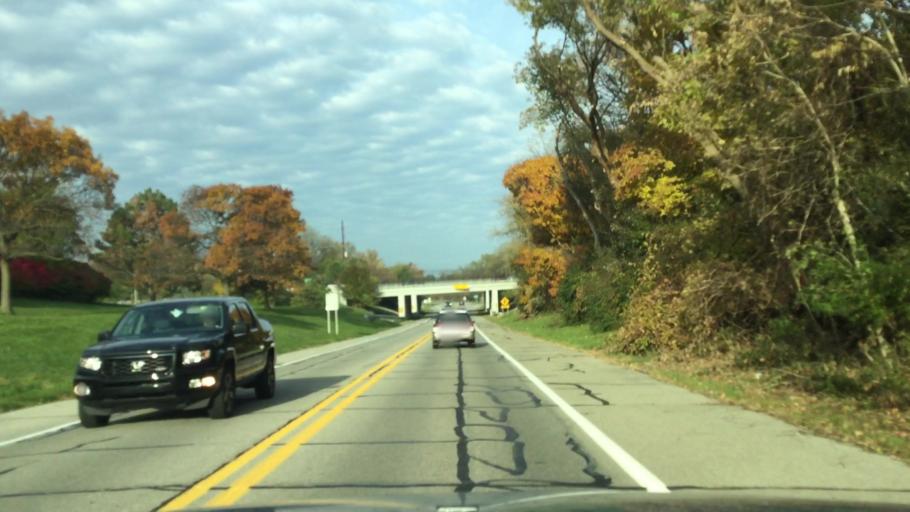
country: US
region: Michigan
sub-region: Wayne County
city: Dearborn Heights
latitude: 42.3455
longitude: -83.2715
